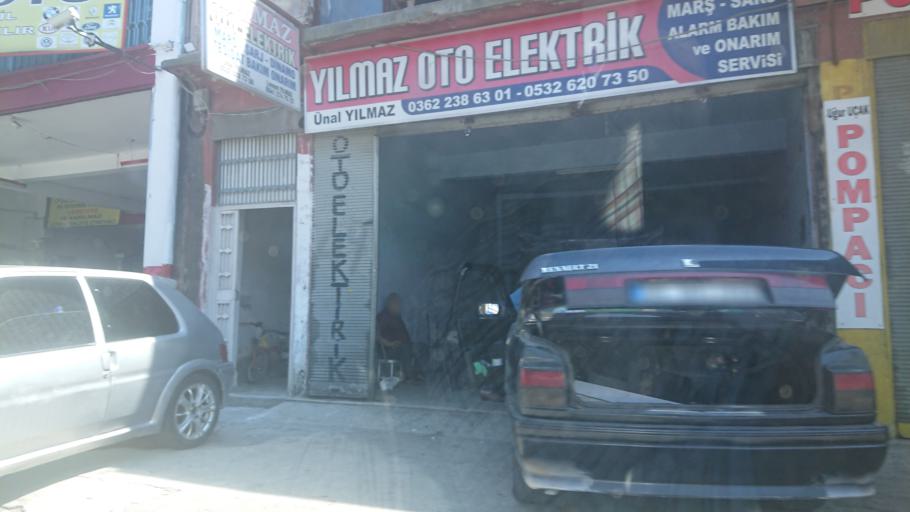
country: TR
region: Samsun
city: Samsun
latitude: 41.2710
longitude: 36.3619
